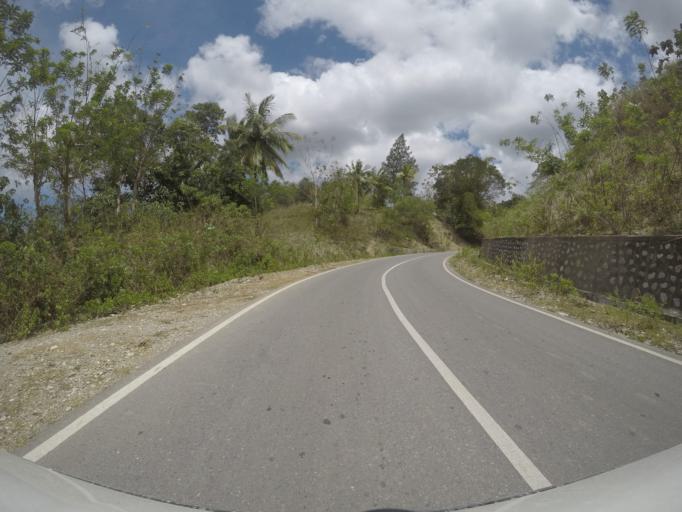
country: TL
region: Viqueque
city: Viqueque
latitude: -8.8760
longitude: 126.3763
